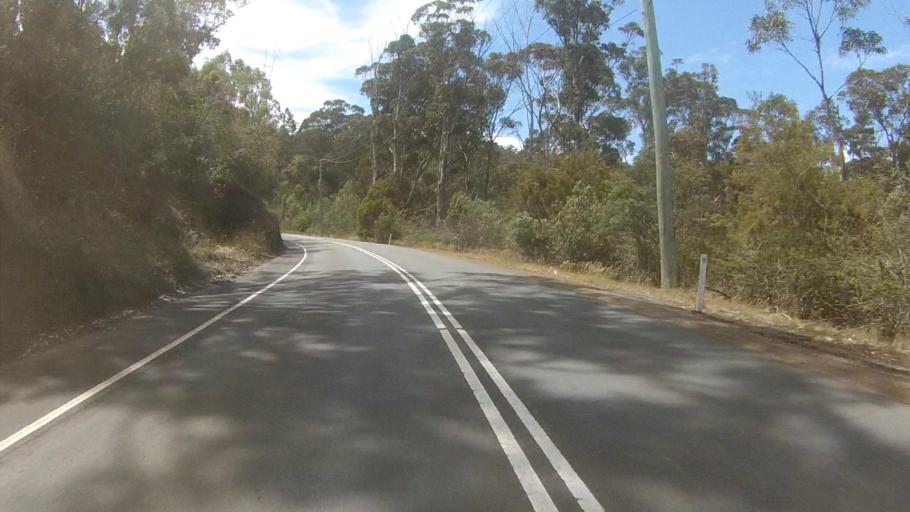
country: AU
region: Tasmania
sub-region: Kingborough
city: Kingston Beach
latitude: -42.9693
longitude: 147.3227
